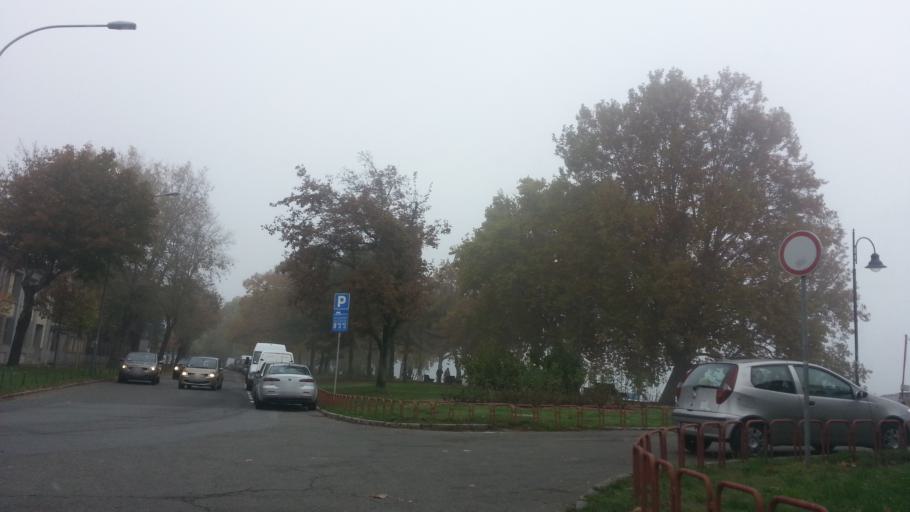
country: RS
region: Central Serbia
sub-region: Belgrade
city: Zemun
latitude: 44.8421
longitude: 20.4174
